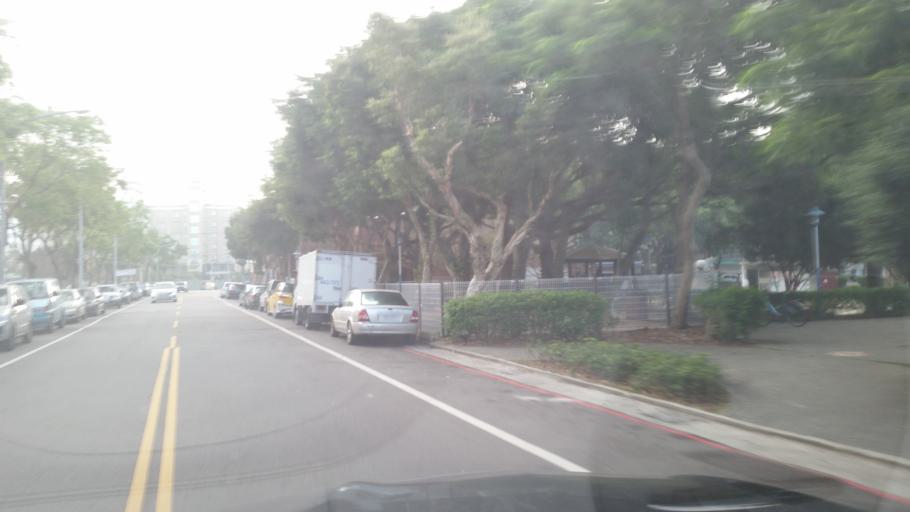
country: TW
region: Taiwan
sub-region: Taoyuan
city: Taoyuan
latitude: 25.0577
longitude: 121.3580
